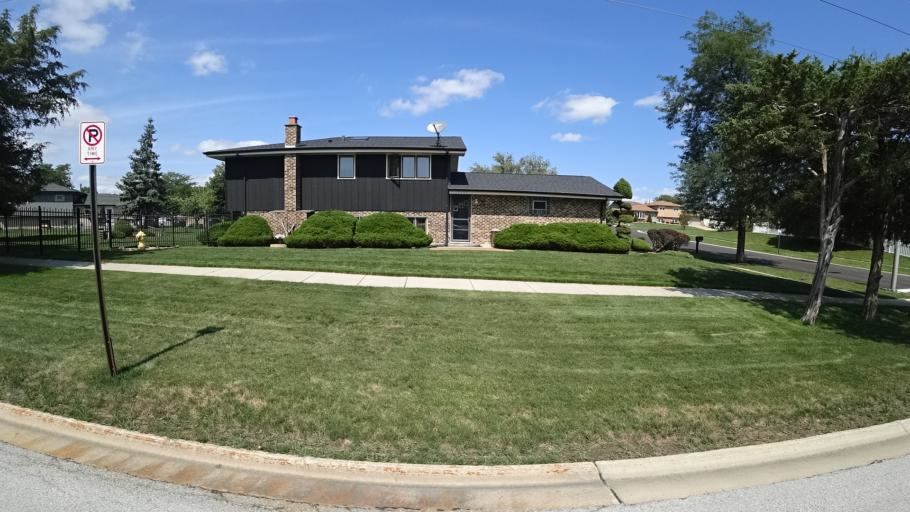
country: US
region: Illinois
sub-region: Cook County
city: Orland Hills
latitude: 41.5726
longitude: -87.8293
